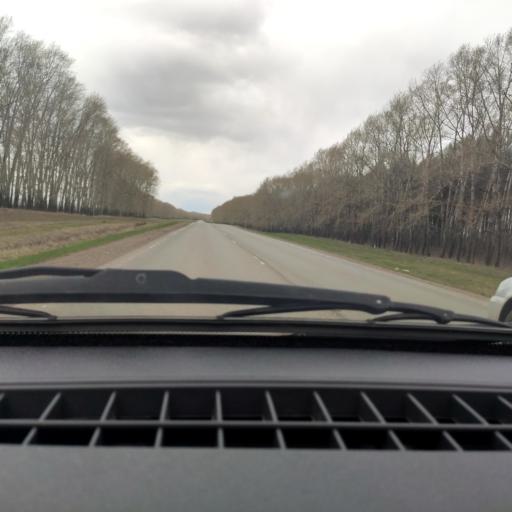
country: RU
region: Bashkortostan
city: Kushnarenkovo
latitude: 55.0835
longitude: 55.3610
